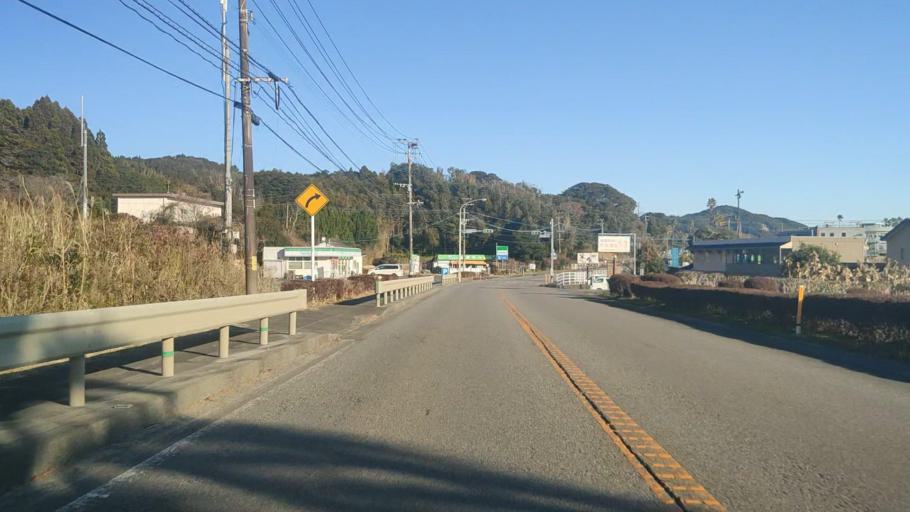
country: JP
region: Miyazaki
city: Nobeoka
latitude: 32.3558
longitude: 131.6211
